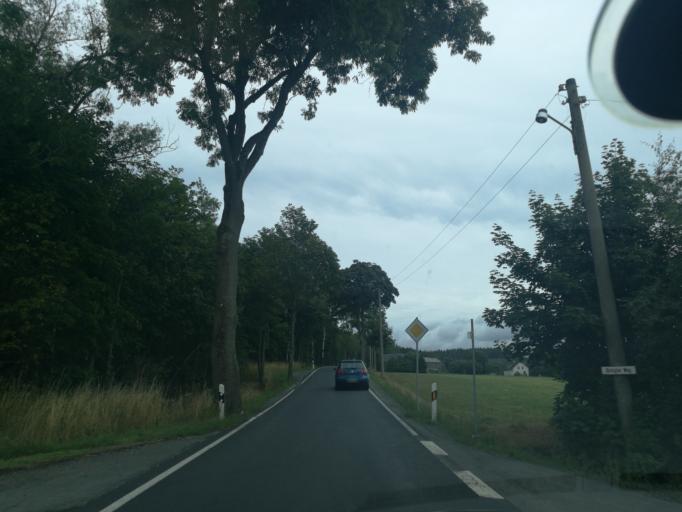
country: DE
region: Saxony
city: Triebel
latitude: 50.3342
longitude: 12.1069
